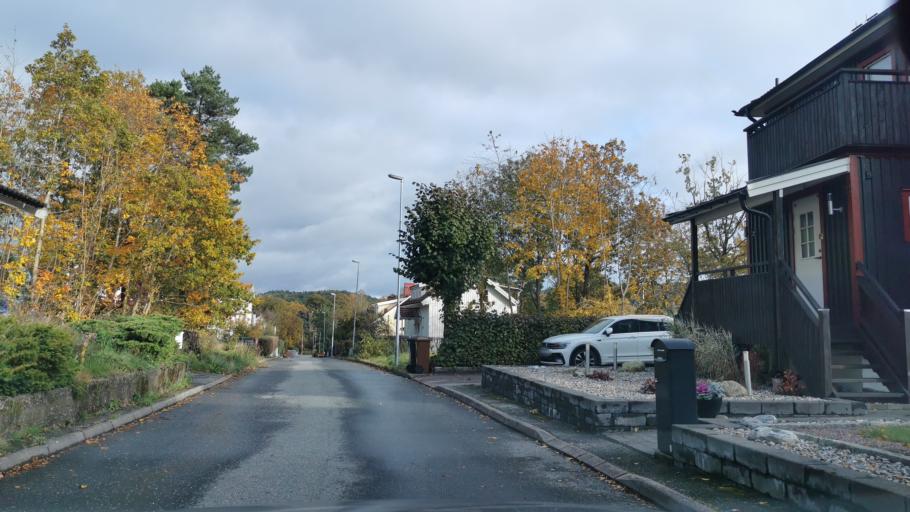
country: SE
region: Vaestra Goetaland
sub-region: Partille Kommun
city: Partille
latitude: 57.7269
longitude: 12.0770
